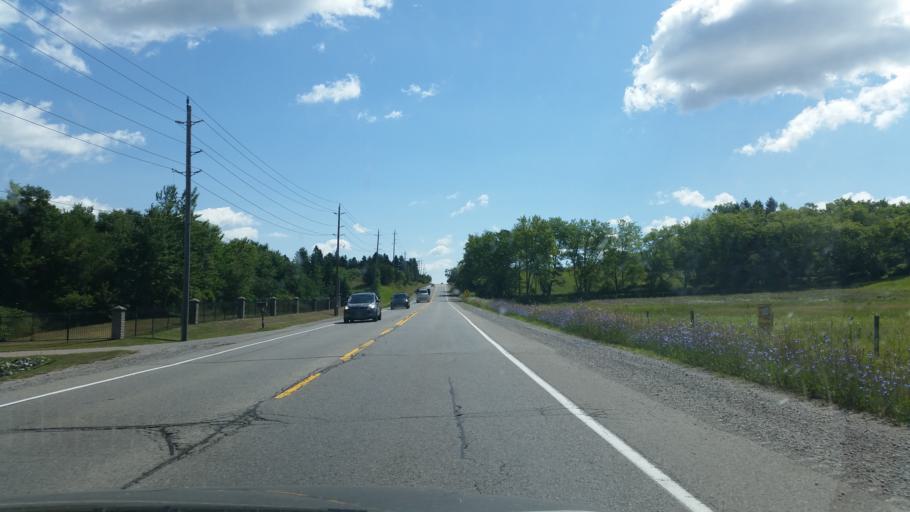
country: CA
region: Ontario
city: Vaughan
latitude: 43.9084
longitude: -79.6226
